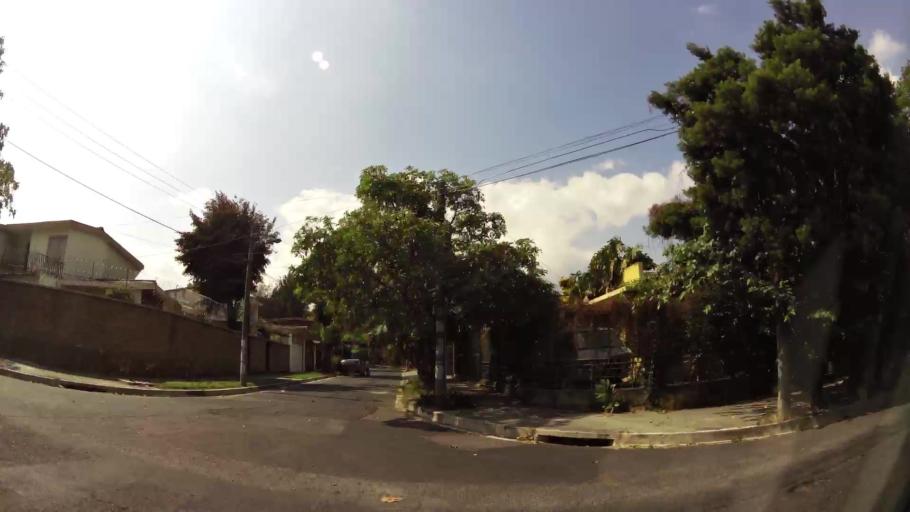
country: SV
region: San Salvador
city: Mejicanos
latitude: 13.7161
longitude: -89.2067
